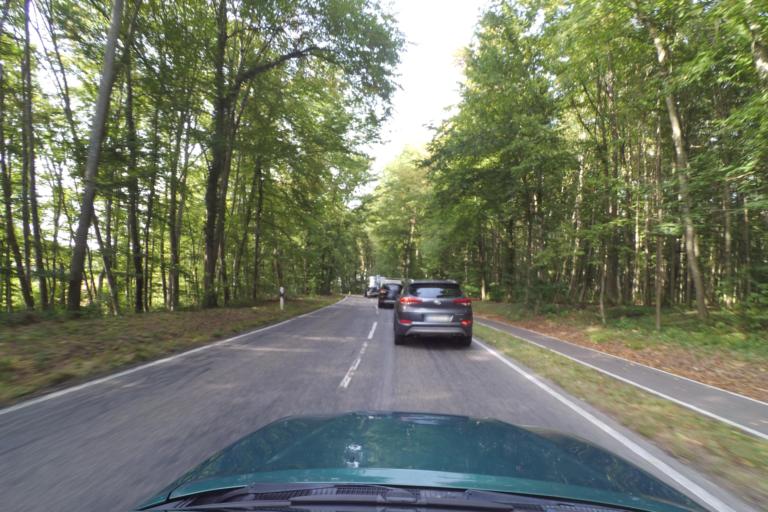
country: DE
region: Baden-Wuerttemberg
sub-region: Freiburg Region
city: Kandern
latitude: 47.7227
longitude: 7.6275
